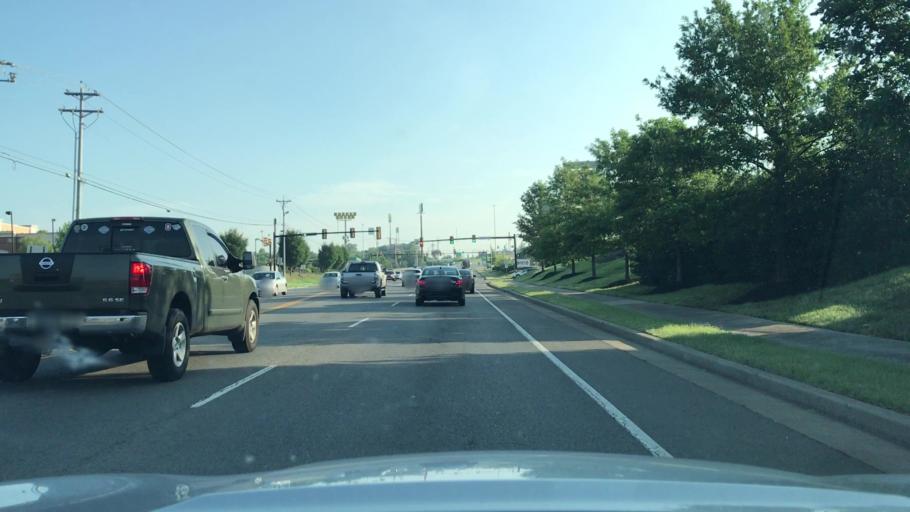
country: US
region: Tennessee
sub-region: Wilson County
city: Mount Juliet
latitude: 36.1651
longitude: -86.5145
